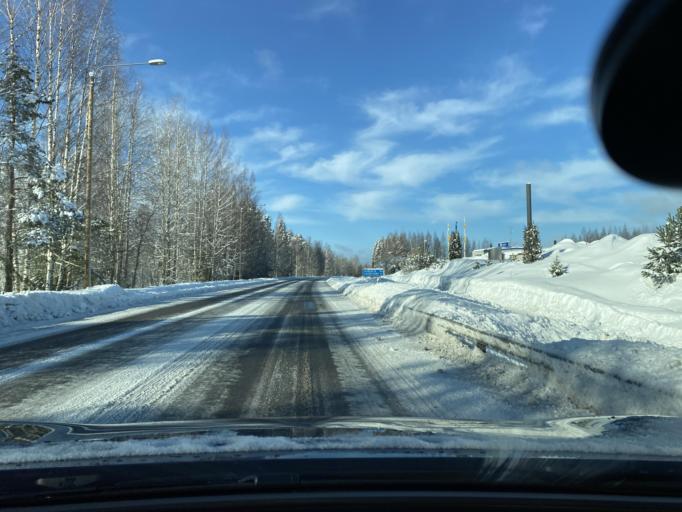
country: FI
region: Southern Savonia
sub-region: Mikkeli
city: Kangasniemi
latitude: 62.0045
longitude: 26.6504
